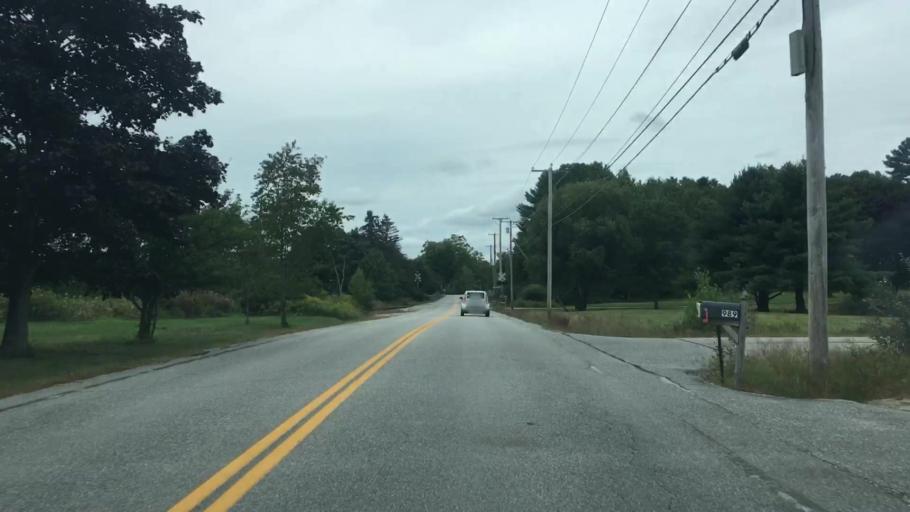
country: US
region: Maine
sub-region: Cumberland County
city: Yarmouth
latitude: 43.8399
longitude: -70.2078
